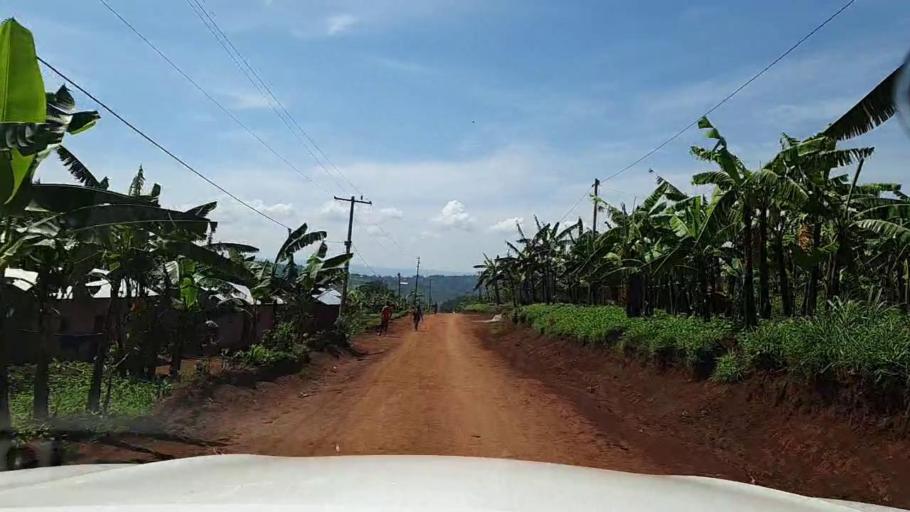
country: RW
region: Southern Province
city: Butare
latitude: -2.7102
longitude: 29.8394
